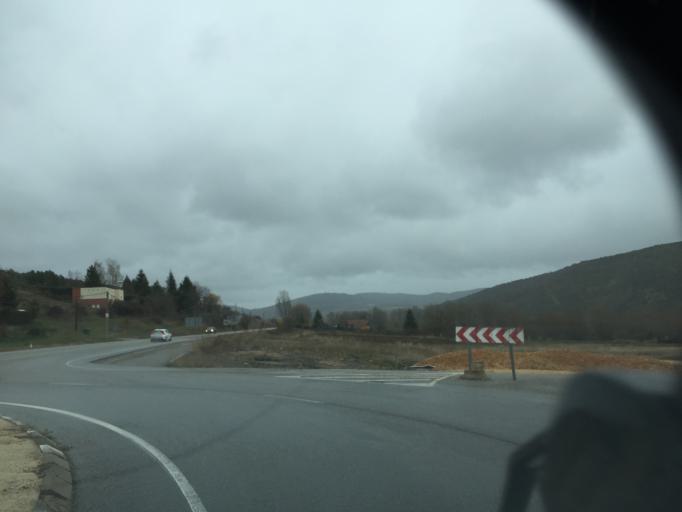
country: ES
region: Castille and Leon
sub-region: Provincia de Leon
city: Carrocera
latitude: 42.7851
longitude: -5.7791
